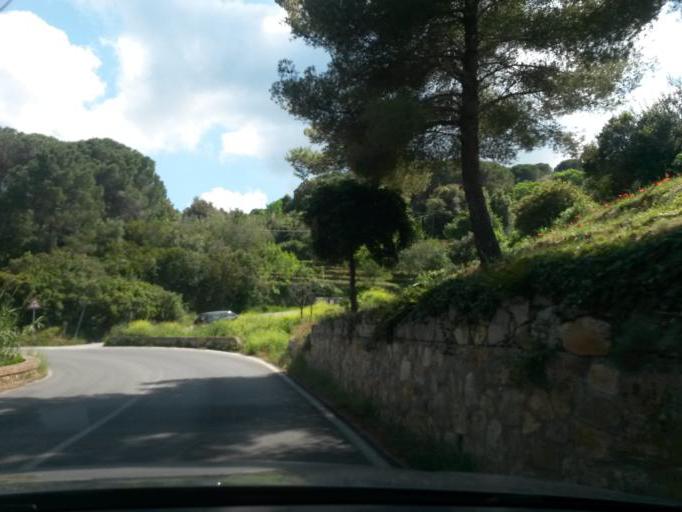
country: IT
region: Tuscany
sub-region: Provincia di Livorno
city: Marciana Marina
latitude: 42.8037
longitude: 10.2087
